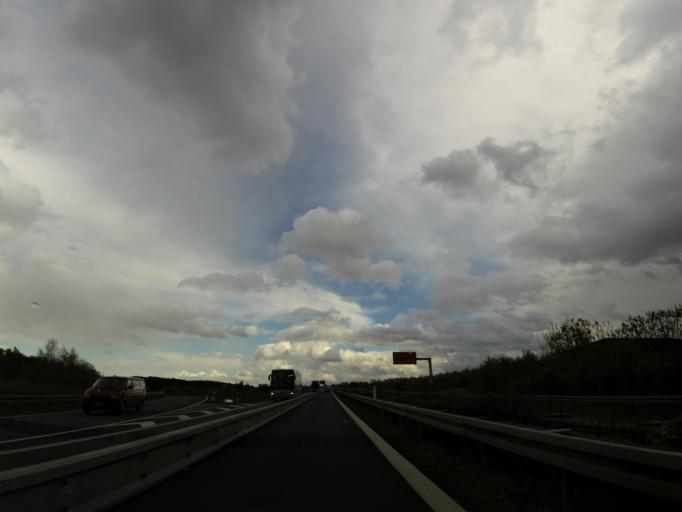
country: DE
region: Saxony-Anhalt
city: Derenburg
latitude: 51.8258
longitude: 10.9233
